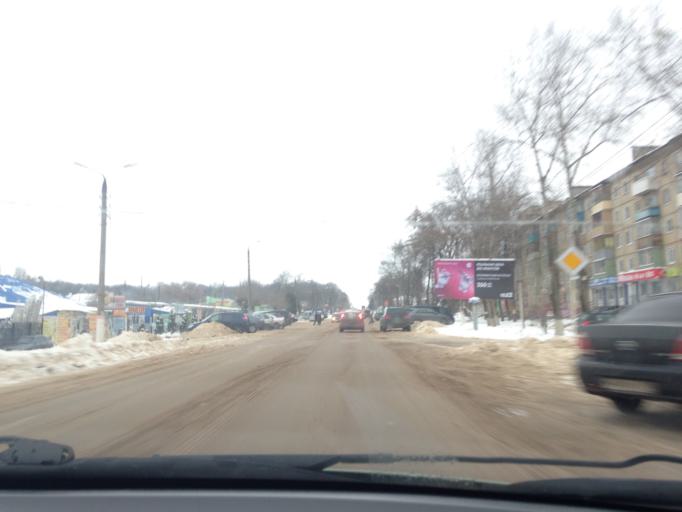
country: RU
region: Tula
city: Shchekino
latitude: 54.0071
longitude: 37.5128
